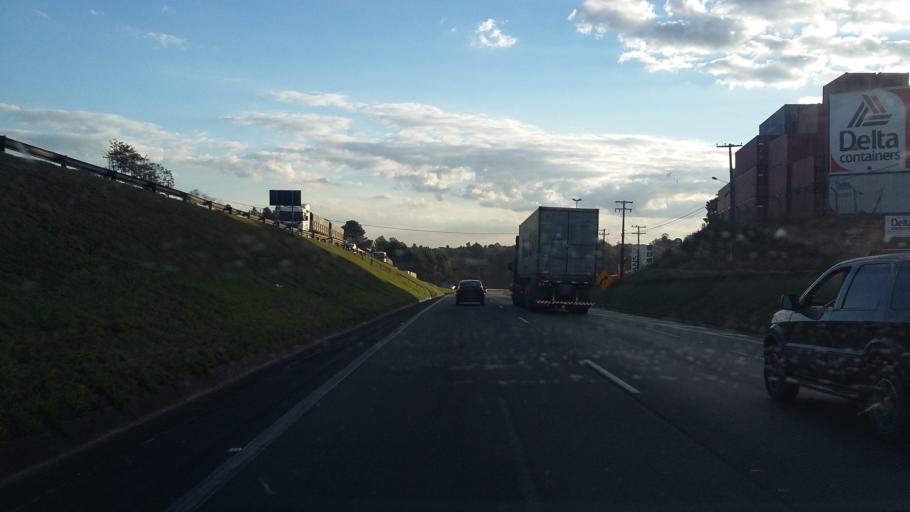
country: BR
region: Parana
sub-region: Campo Largo
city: Campo Largo
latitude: -25.4341
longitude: -49.4105
